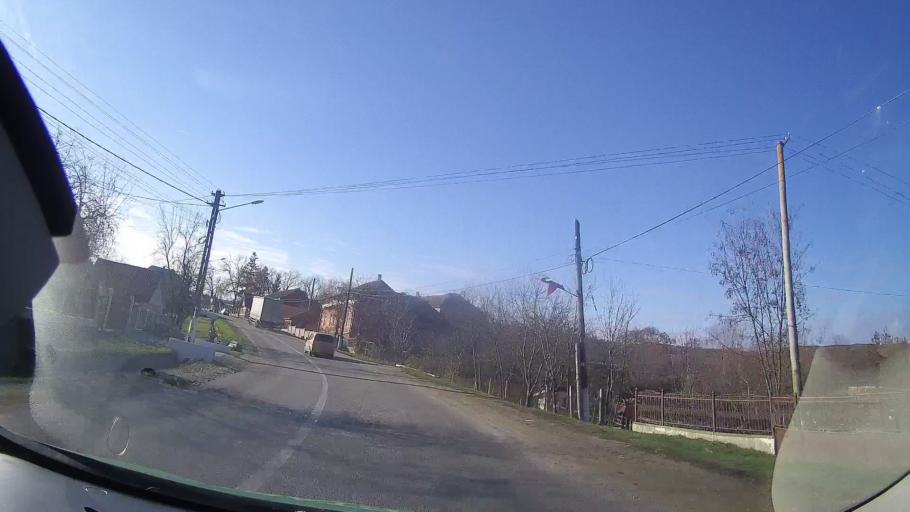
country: RO
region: Cluj
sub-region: Comuna Mociu
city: Mociu
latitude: 46.8001
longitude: 24.0386
